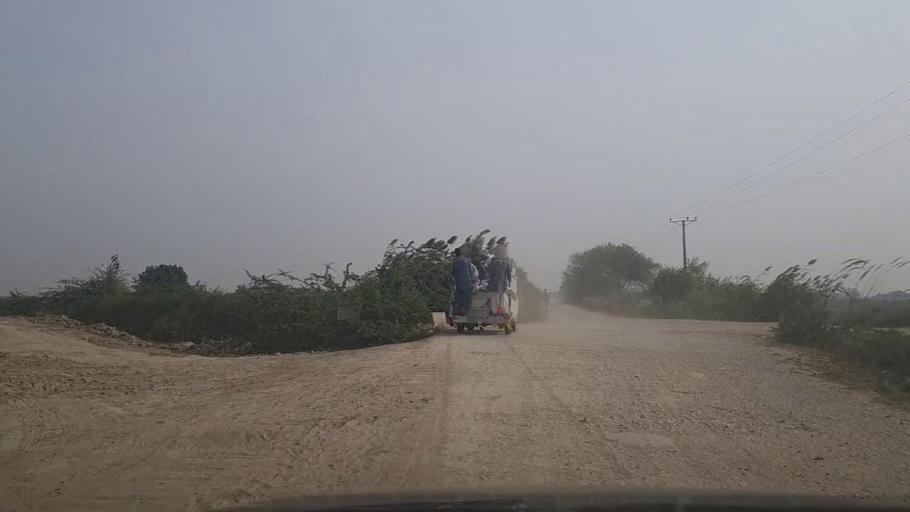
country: PK
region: Sindh
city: Mirpur Sakro
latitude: 24.4738
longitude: 67.6688
